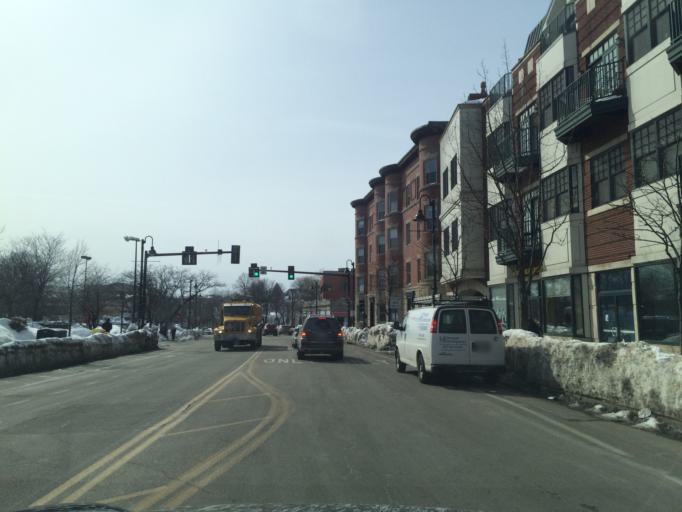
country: US
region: Massachusetts
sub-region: Norfolk County
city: Brookline
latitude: 42.3387
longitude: -71.1213
